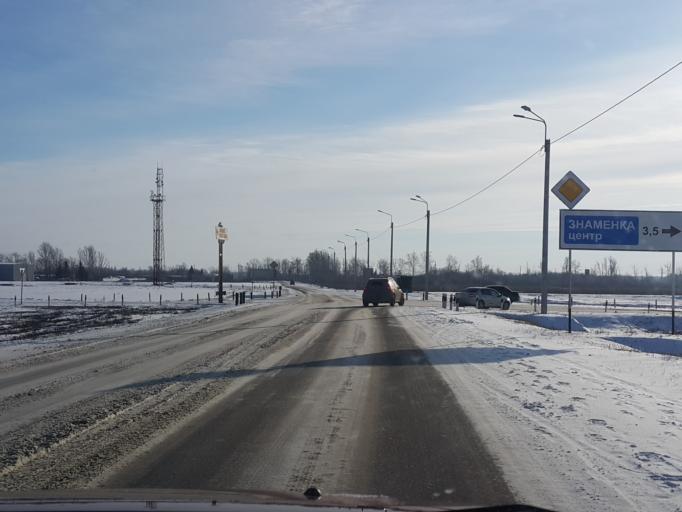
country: RU
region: Tambov
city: Znamenka
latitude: 52.4254
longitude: 41.5044
